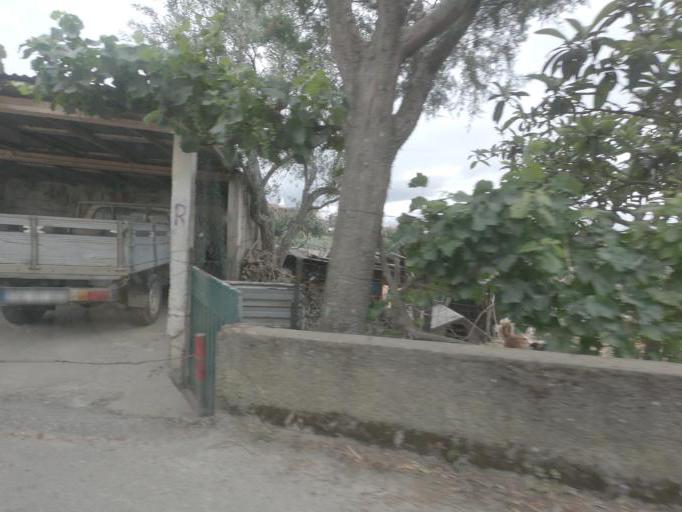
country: PT
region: Vila Real
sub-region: Sabrosa
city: Sabrosa
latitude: 41.2250
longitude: -7.5026
